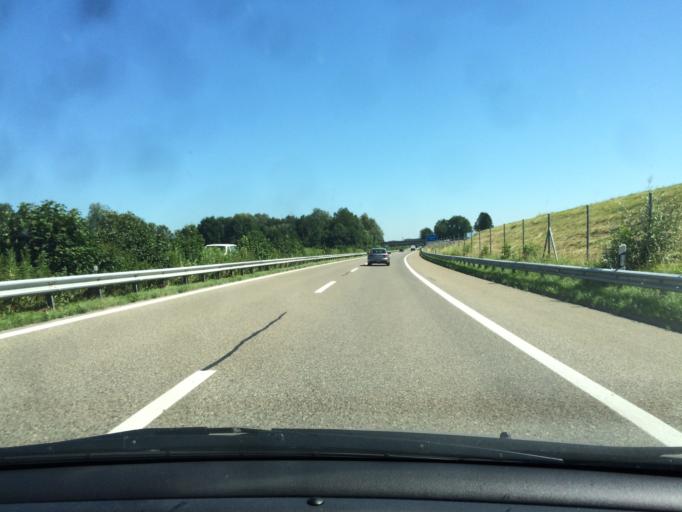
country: AT
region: Vorarlberg
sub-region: Politischer Bezirk Feldkirch
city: Koblach
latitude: 47.3456
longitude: 9.5968
